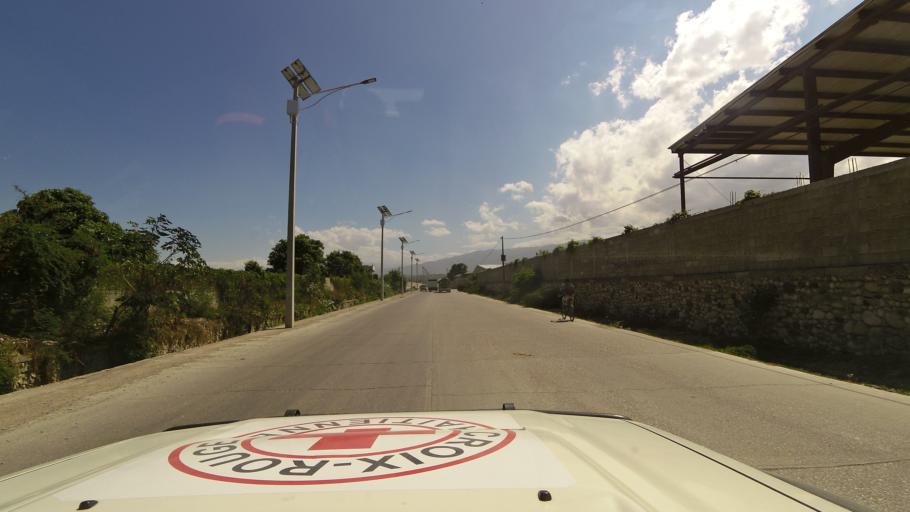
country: HT
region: Ouest
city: Delmas 73
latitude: 18.5894
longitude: -72.3202
